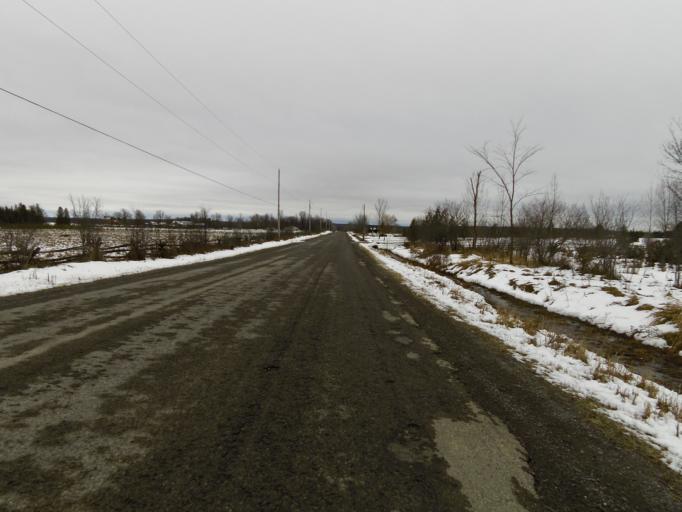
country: CA
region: Ontario
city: Carleton Place
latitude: 45.2904
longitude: -76.2316
